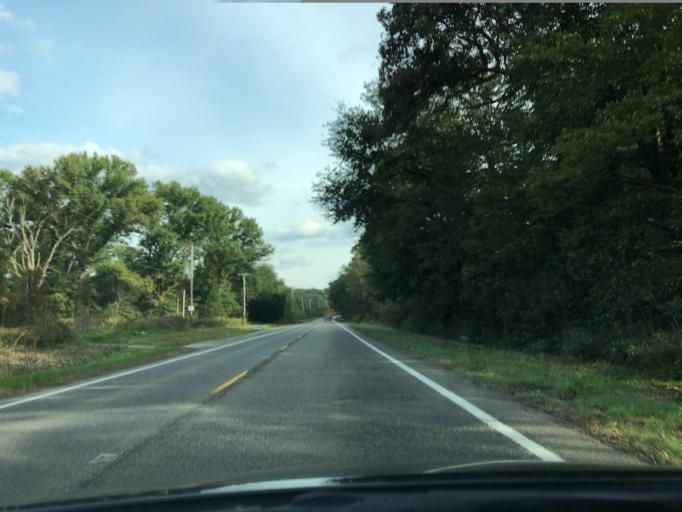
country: US
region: Ohio
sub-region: Stark County
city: Beach City
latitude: 40.6367
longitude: -81.5678
